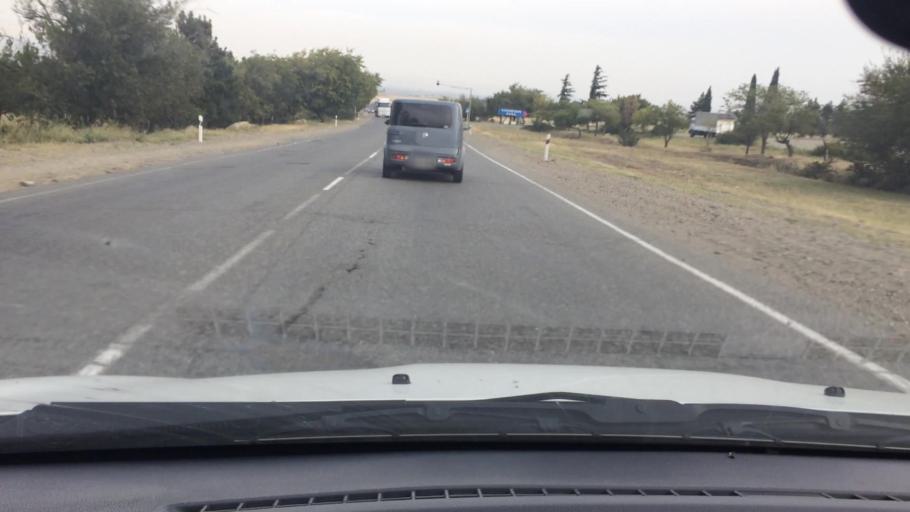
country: GE
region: T'bilisi
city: Tbilisi
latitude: 41.6399
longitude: 44.8668
